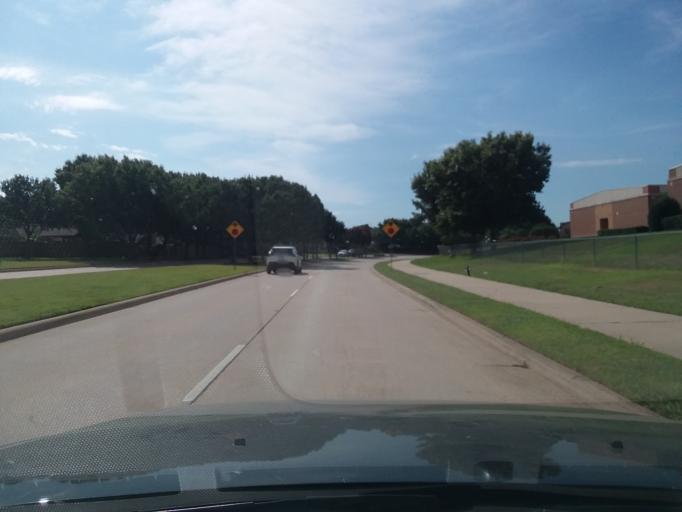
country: US
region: Texas
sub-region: Denton County
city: Flower Mound
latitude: 33.0313
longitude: -97.0922
